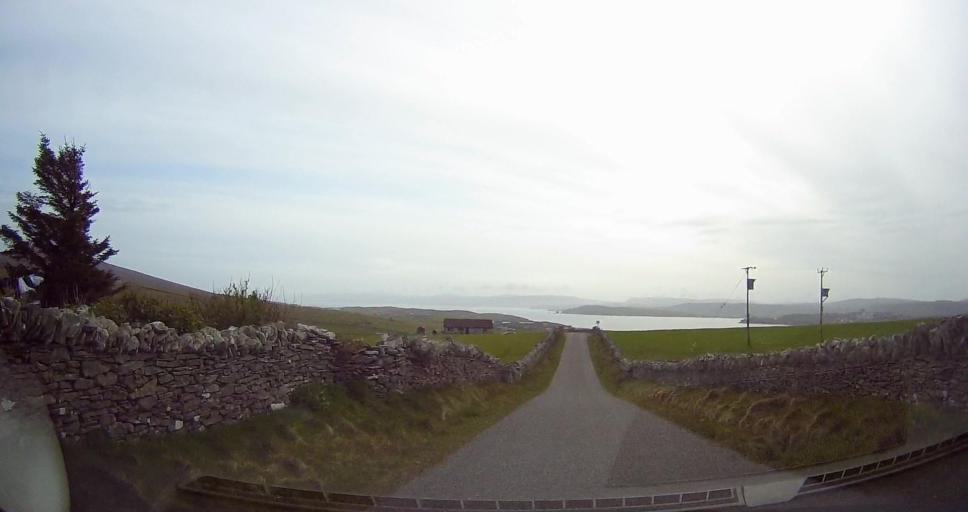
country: GB
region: Scotland
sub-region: Shetland Islands
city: Shetland
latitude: 60.1524
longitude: -1.0960
